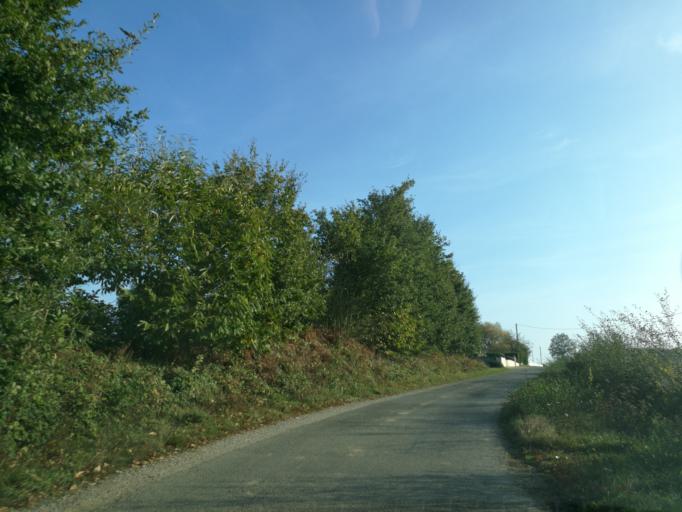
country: FR
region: Brittany
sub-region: Departement d'Ille-et-Vilaine
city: Pleumeleuc
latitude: 48.1724
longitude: -1.9027
